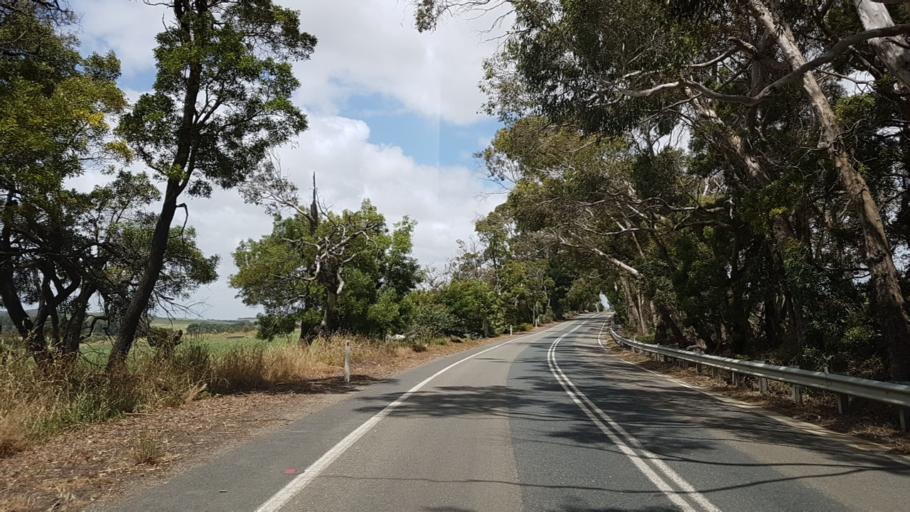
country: AU
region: South Australia
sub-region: Alexandrina
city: Mount Compass
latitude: -35.4186
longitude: 138.5616
